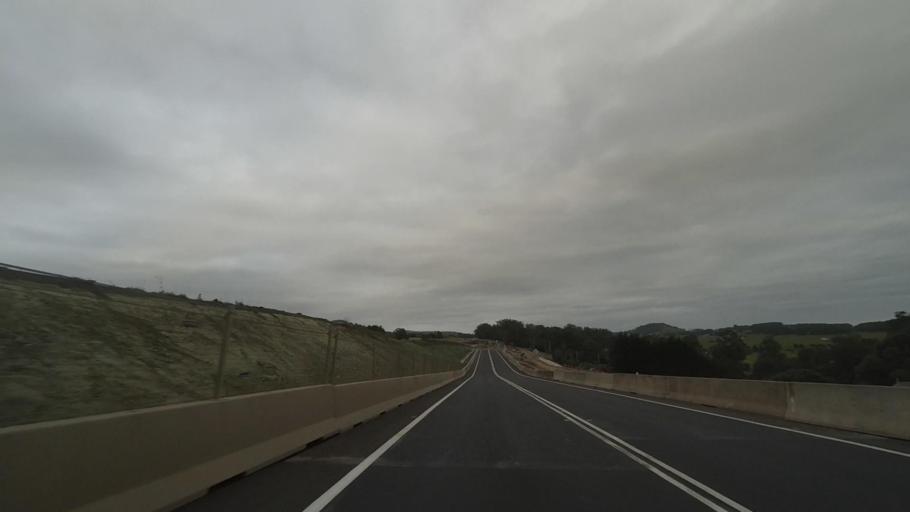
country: AU
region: New South Wales
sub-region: Shoalhaven Shire
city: Berry
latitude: -34.7703
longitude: 150.7091
